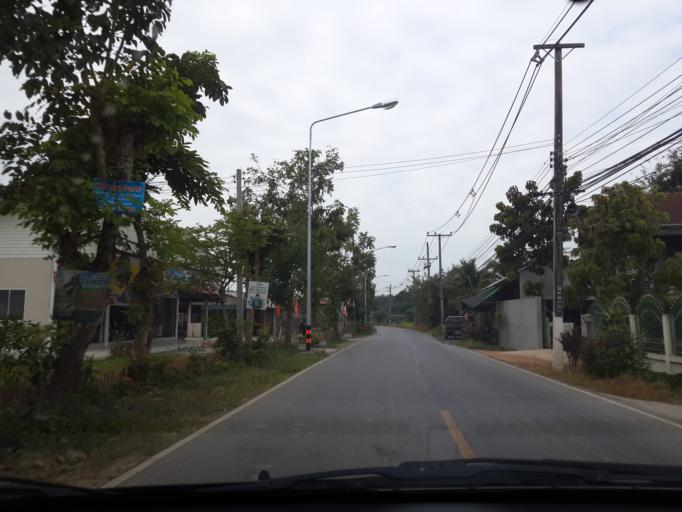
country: TH
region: Chiang Mai
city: San Sai
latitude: 18.8919
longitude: 99.0913
